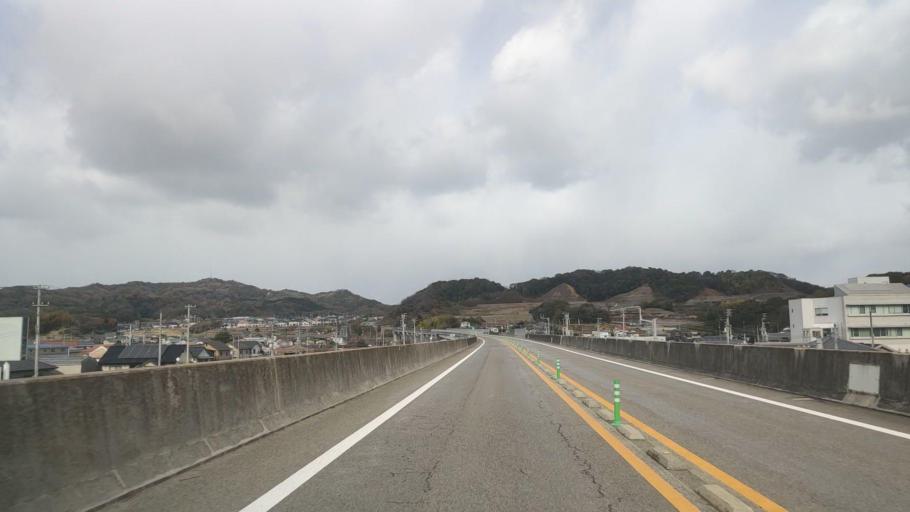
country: JP
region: Ehime
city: Hojo
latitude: 34.0595
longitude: 132.9717
